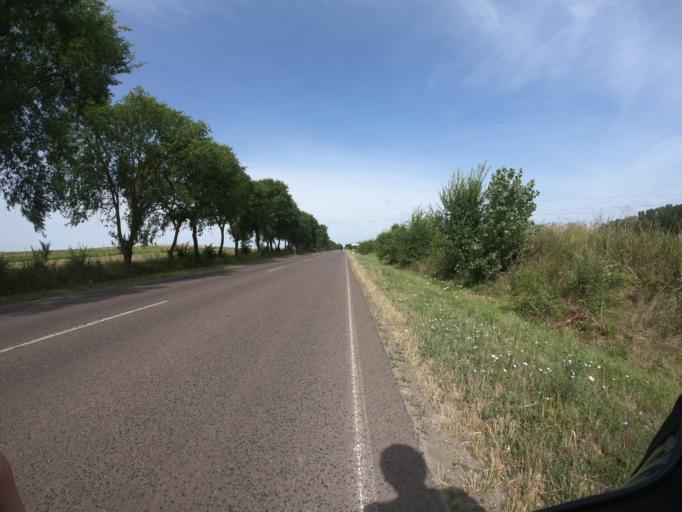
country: HU
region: Jasz-Nagykun-Szolnok
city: Tiszafured
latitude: 47.6004
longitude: 20.8029
